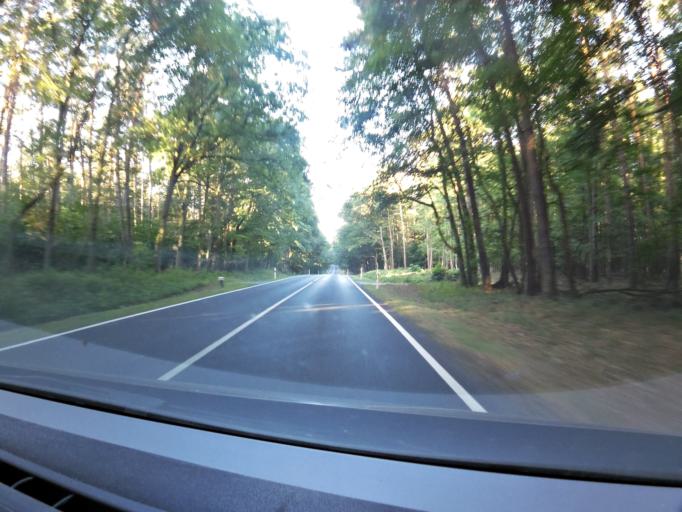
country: DE
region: Mecklenburg-Vorpommern
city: Usedom
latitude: 53.9053
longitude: 14.0039
